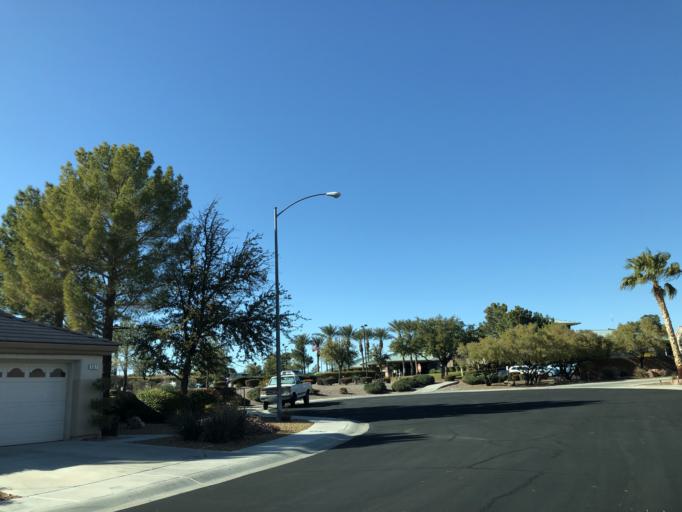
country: US
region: Nevada
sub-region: Clark County
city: Whitney
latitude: 36.0054
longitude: -115.0753
